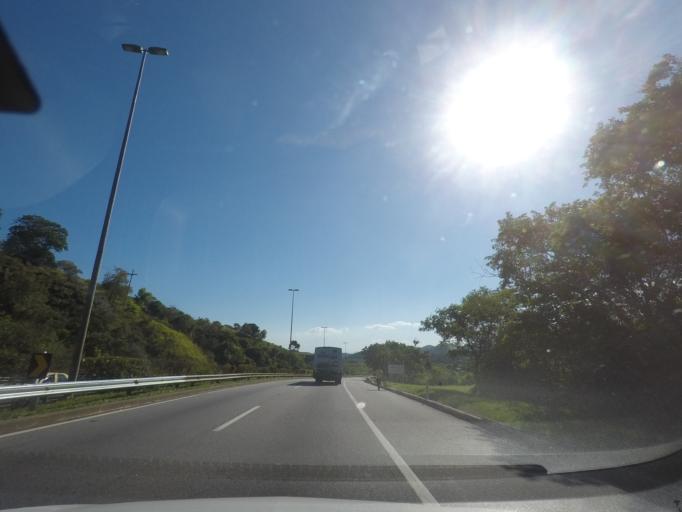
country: BR
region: Rio de Janeiro
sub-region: Sao Goncalo
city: Sao Goncalo
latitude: -22.6639
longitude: -43.0954
